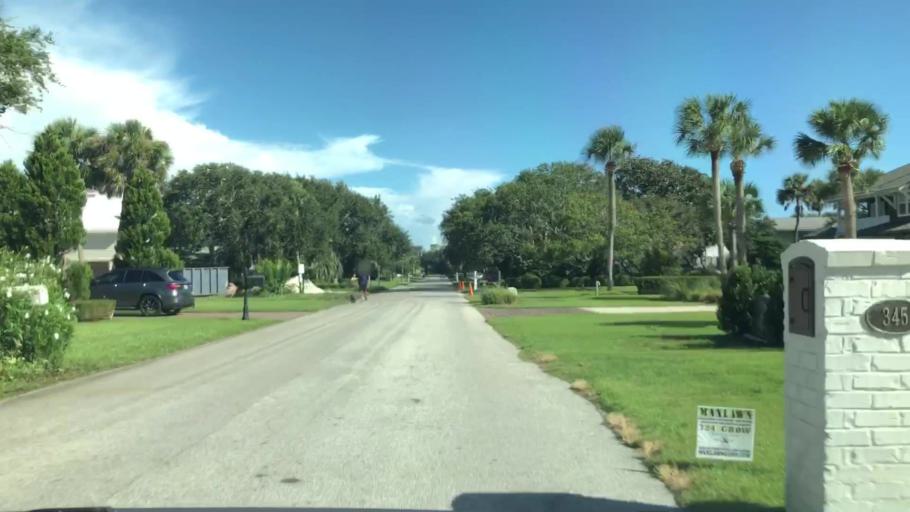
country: US
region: Florida
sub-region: Saint Johns County
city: Ponte Vedra Beach
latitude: 30.2321
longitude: -81.3795
